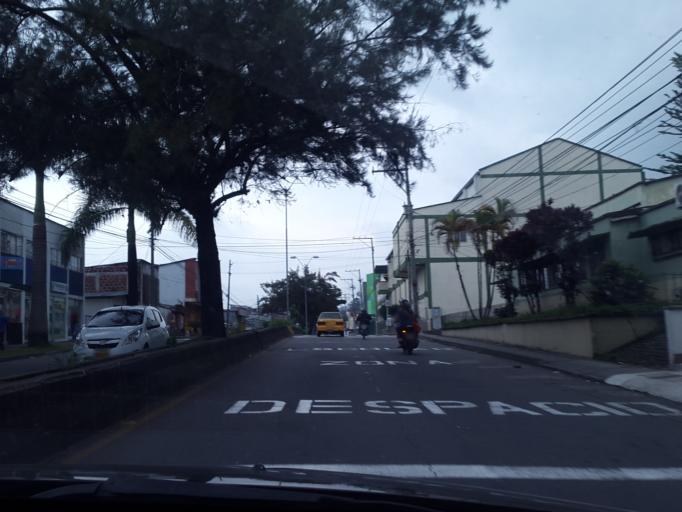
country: CO
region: Quindio
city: Armenia
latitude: 4.5433
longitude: -75.6711
